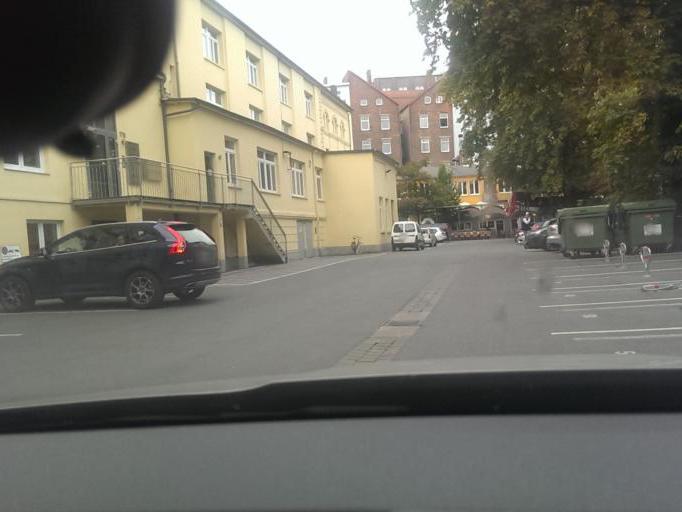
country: DE
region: Lower Saxony
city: Hannover
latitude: 52.3668
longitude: 9.7208
